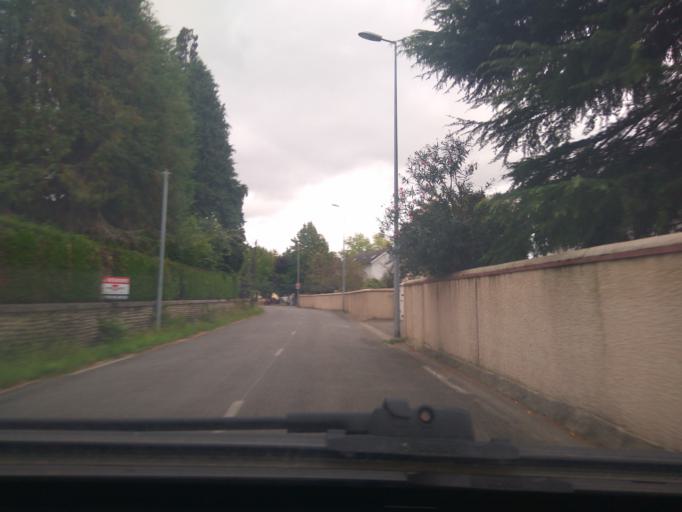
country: FR
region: Aquitaine
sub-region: Departement des Pyrenees-Atlantiques
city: Bizanos
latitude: 43.2978
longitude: -0.3337
